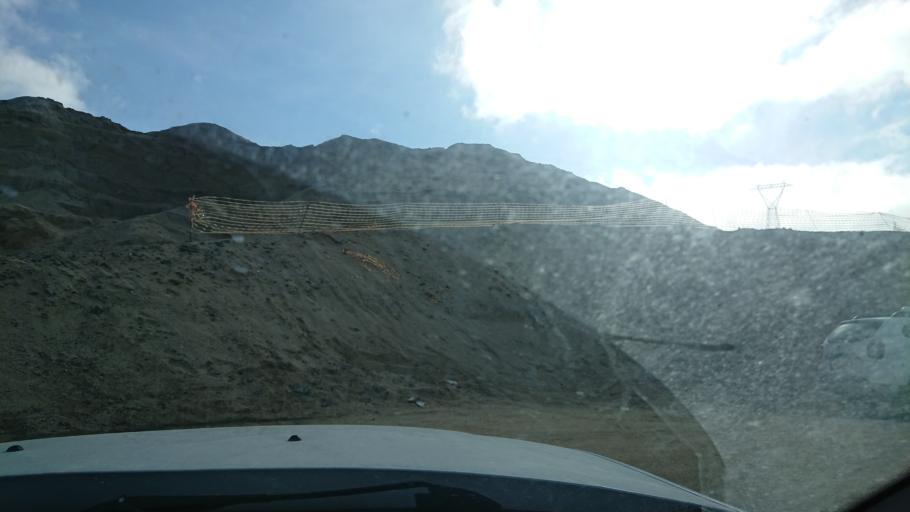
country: TR
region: Aksaray
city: Agacoren
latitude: 38.8461
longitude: 33.9443
